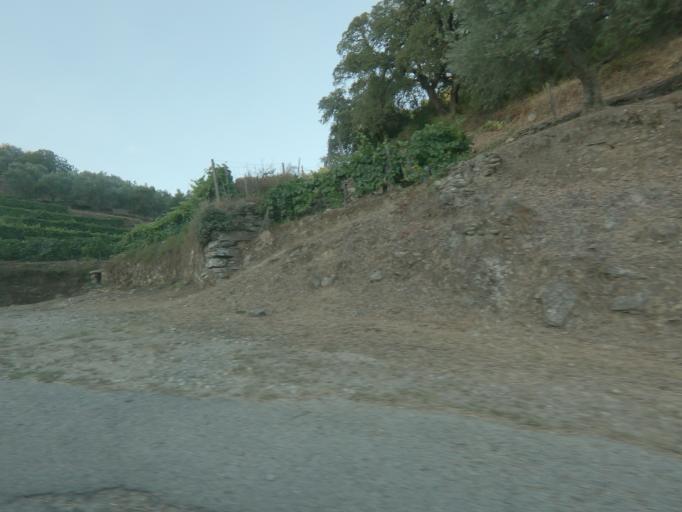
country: PT
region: Viseu
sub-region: Armamar
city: Armamar
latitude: 41.1814
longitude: -7.6886
